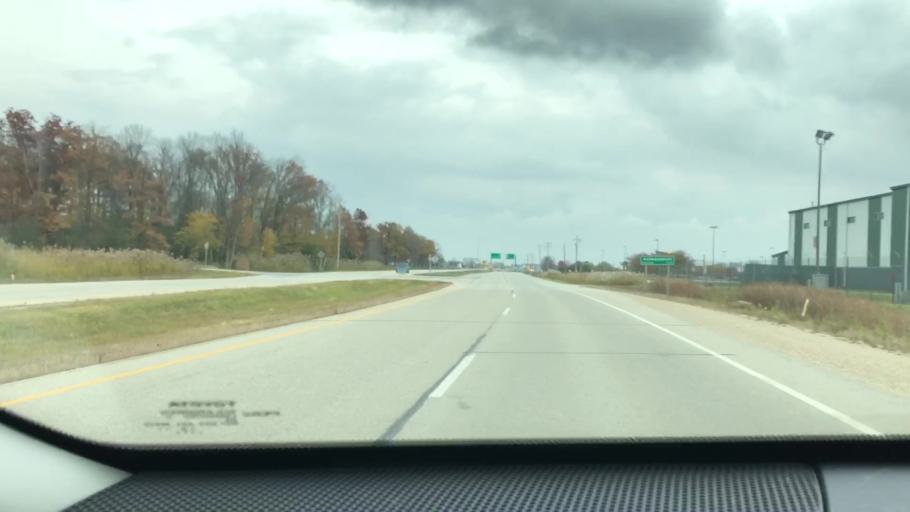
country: US
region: Wisconsin
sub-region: Brown County
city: Oneida
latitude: 44.4956
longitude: -88.1310
